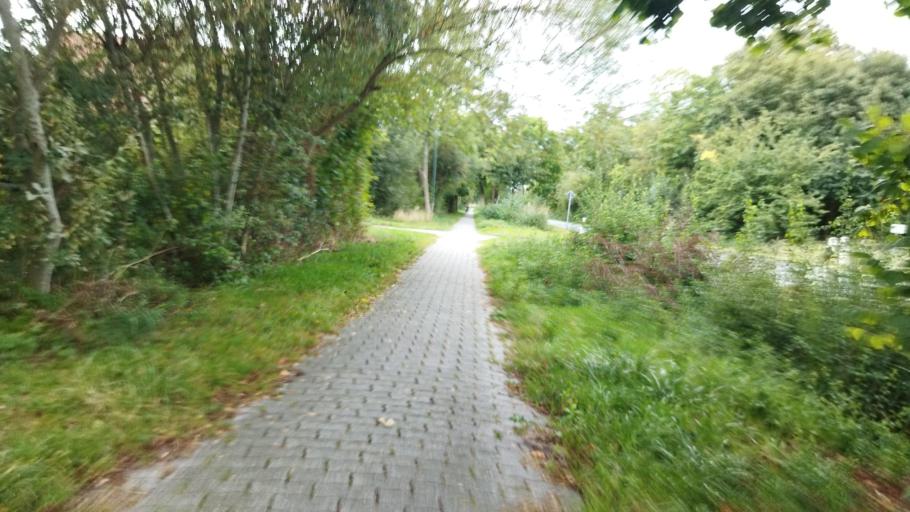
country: DE
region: Lower Saxony
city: Hinte
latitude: 53.4205
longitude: 7.1873
